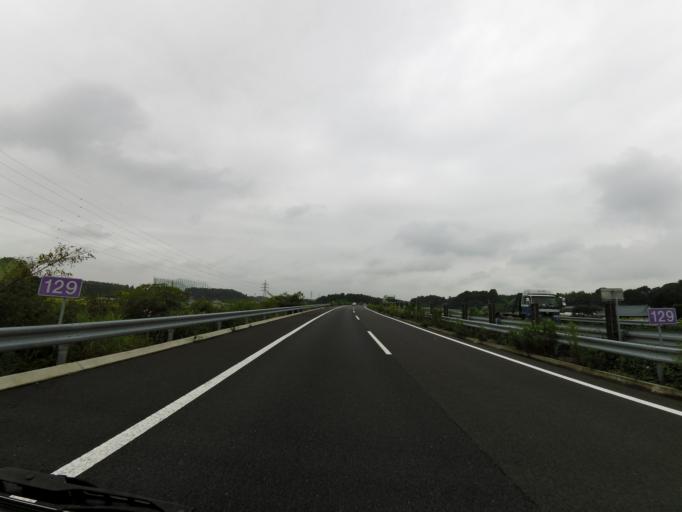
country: JP
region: Tochigi
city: Mooka
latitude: 36.4220
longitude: 139.9832
